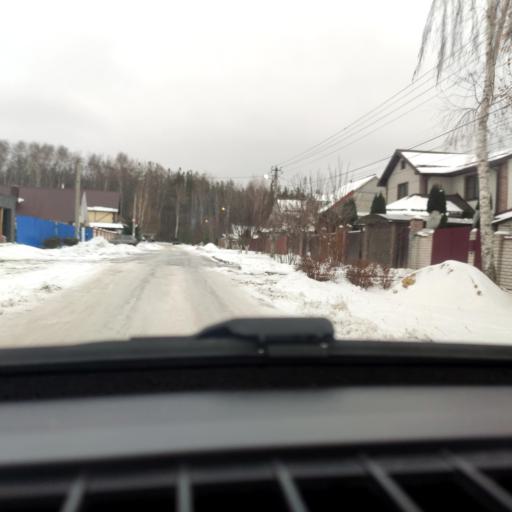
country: RU
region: Voronezj
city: Somovo
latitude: 51.6879
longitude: 39.3096
